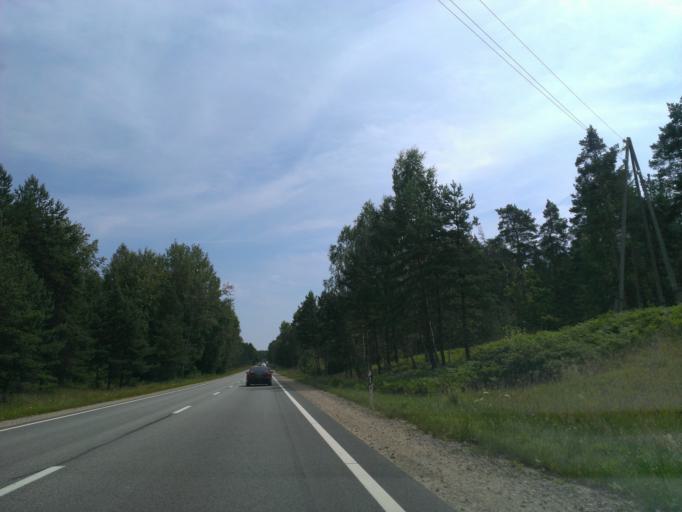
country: LV
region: Riga
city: Bergi
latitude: 56.9692
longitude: 24.3521
